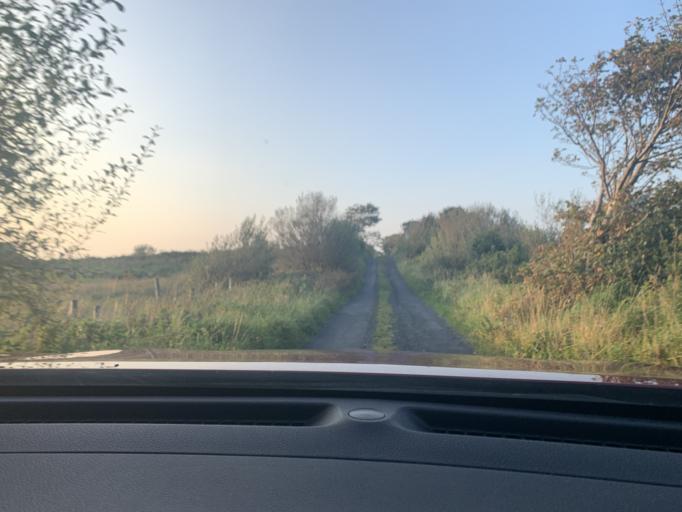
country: IE
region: Connaught
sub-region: County Leitrim
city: Kinlough
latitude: 54.4560
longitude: -8.3980
